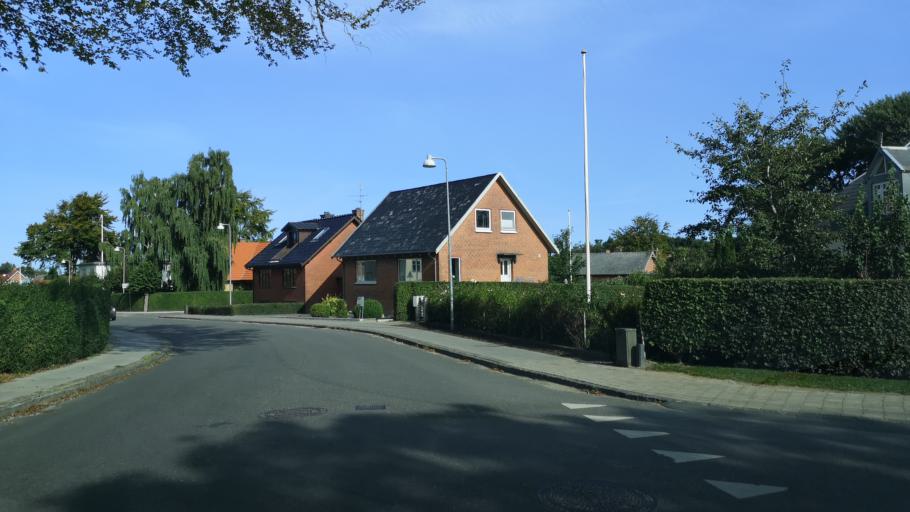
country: DK
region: Central Jutland
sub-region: Ikast-Brande Kommune
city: Ikast
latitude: 56.1453
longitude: 9.1537
